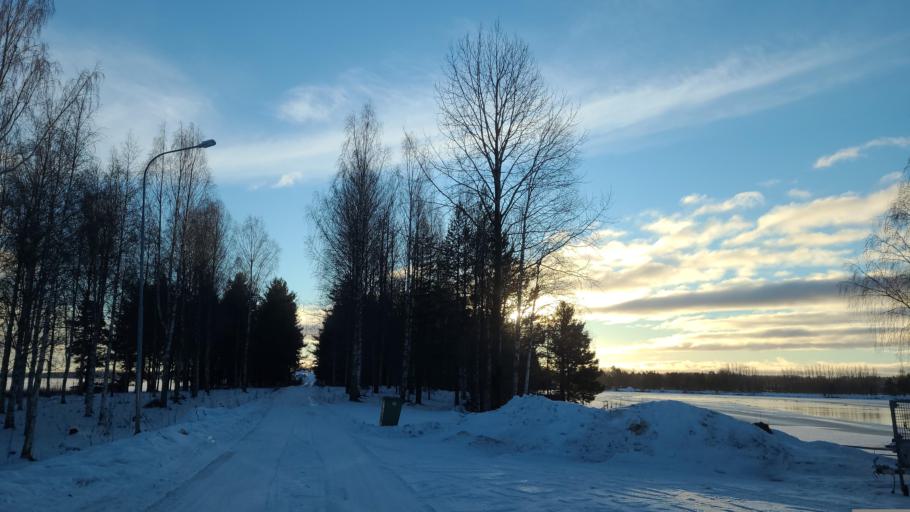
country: SE
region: Gaevleborg
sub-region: Bollnas Kommun
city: Bollnas
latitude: 61.3519
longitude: 16.4083
